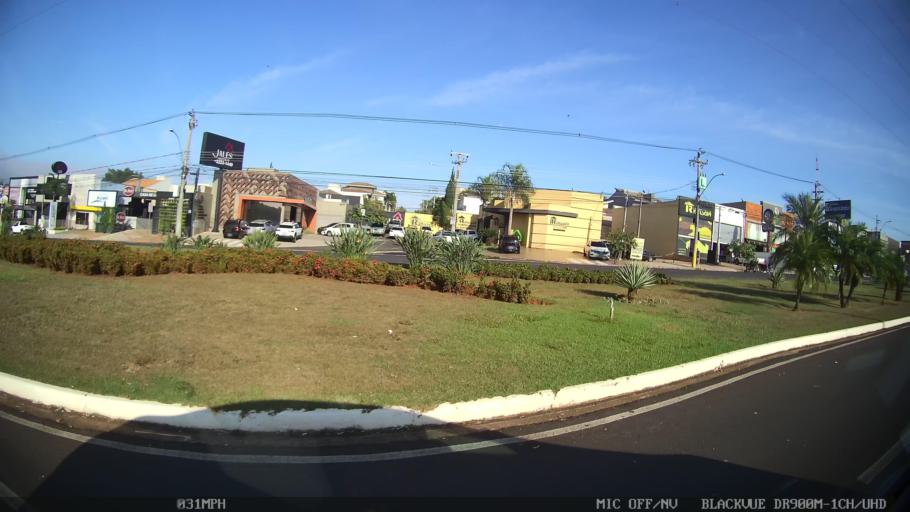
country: BR
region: Sao Paulo
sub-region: Sao Jose Do Rio Preto
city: Sao Jose do Rio Preto
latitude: -20.8055
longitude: -49.3435
